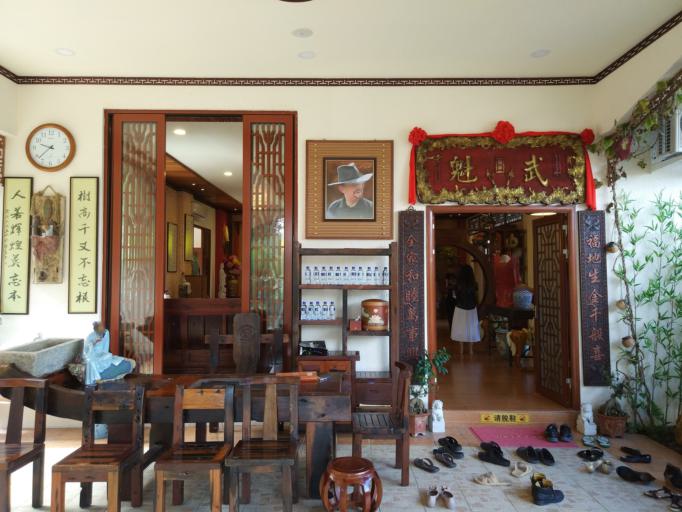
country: BN
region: Brunei and Muara
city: Bandar Seri Begawan
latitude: 4.8909
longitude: 114.9681
